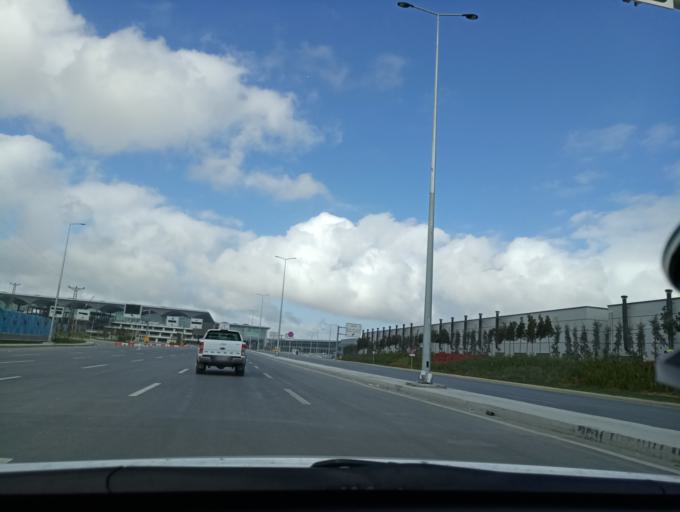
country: TR
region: Istanbul
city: Durusu
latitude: 41.2530
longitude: 28.7465
